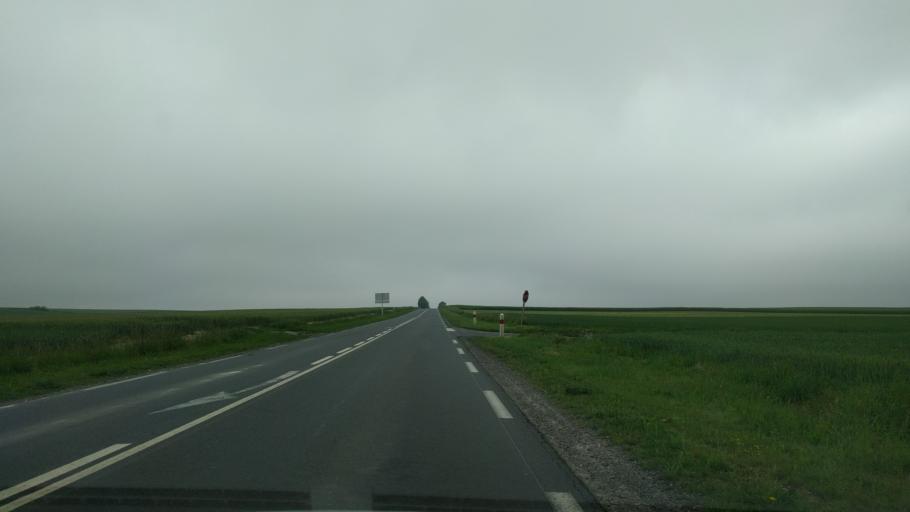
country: FR
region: Picardie
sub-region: Departement de la Somme
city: Moislains
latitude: 49.9879
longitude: 2.9143
